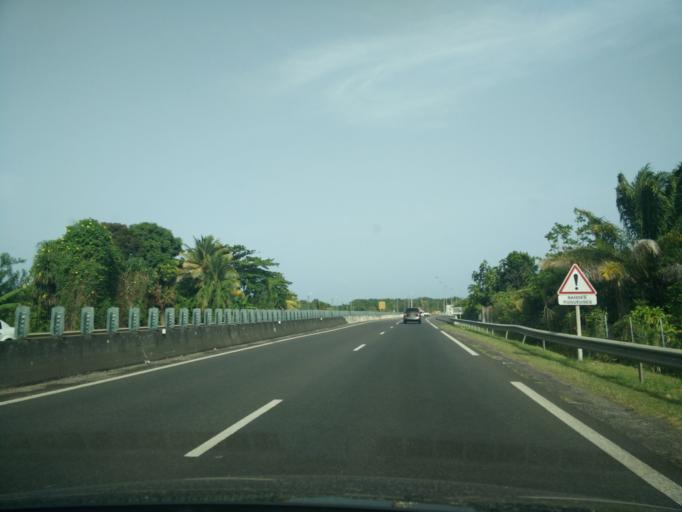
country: GP
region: Guadeloupe
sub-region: Guadeloupe
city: Petit-Bourg
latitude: 16.1748
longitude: -61.5905
